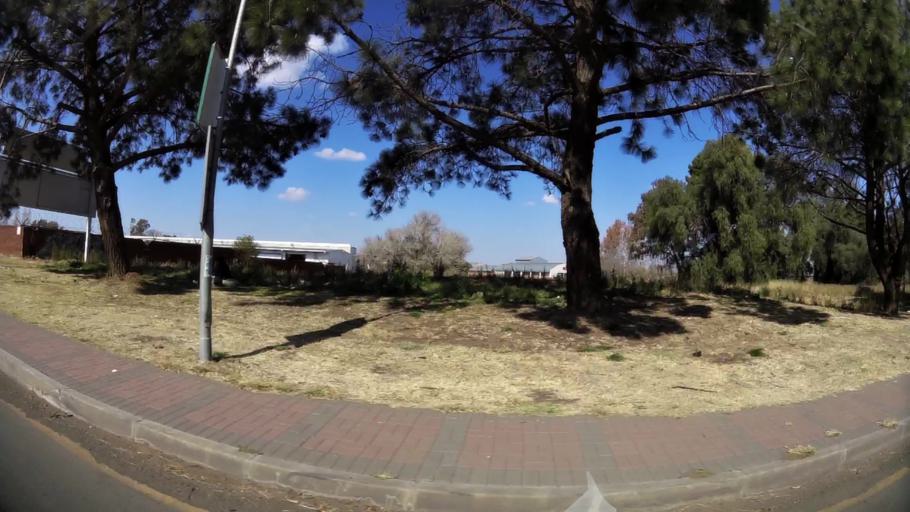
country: ZA
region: Orange Free State
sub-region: Mangaung Metropolitan Municipality
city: Bloemfontein
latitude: -29.1186
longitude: 26.2345
